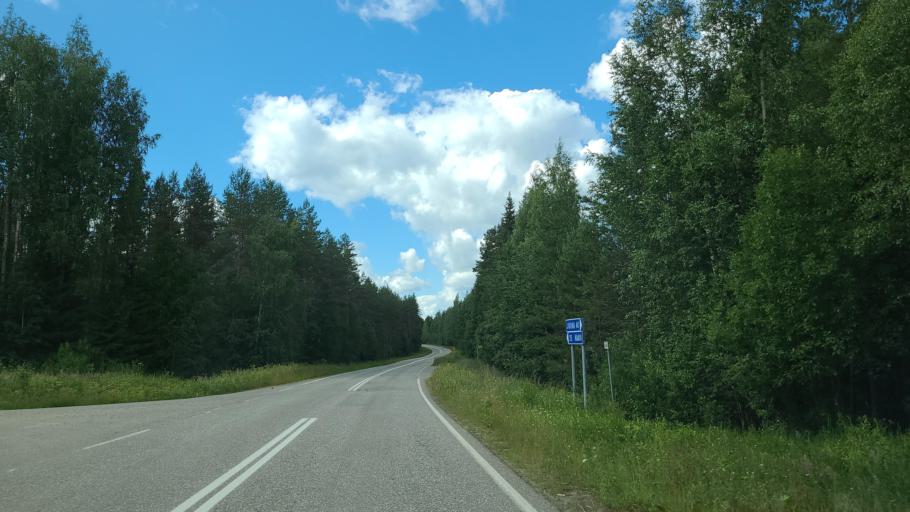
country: FI
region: North Karelia
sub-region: Joensuu
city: Outokumpu
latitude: 62.9890
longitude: 28.8250
